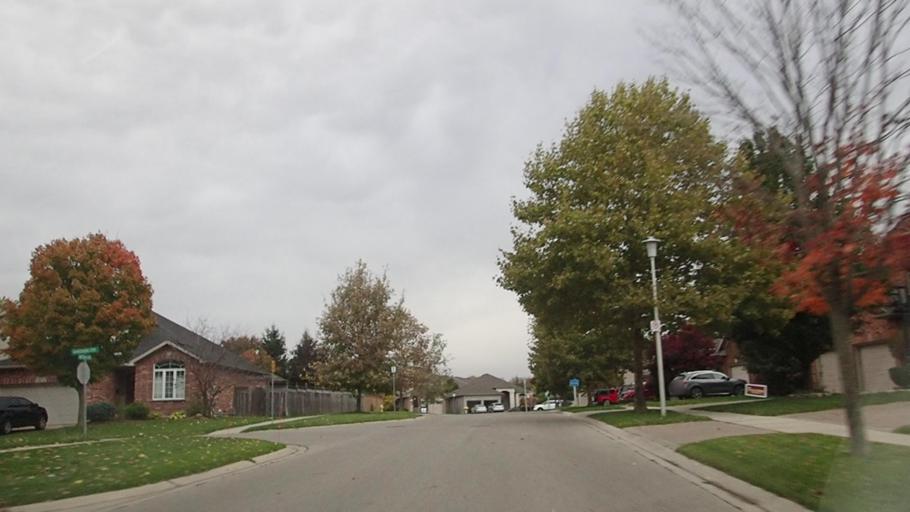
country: CA
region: Ontario
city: London
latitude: 43.0392
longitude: -81.2667
